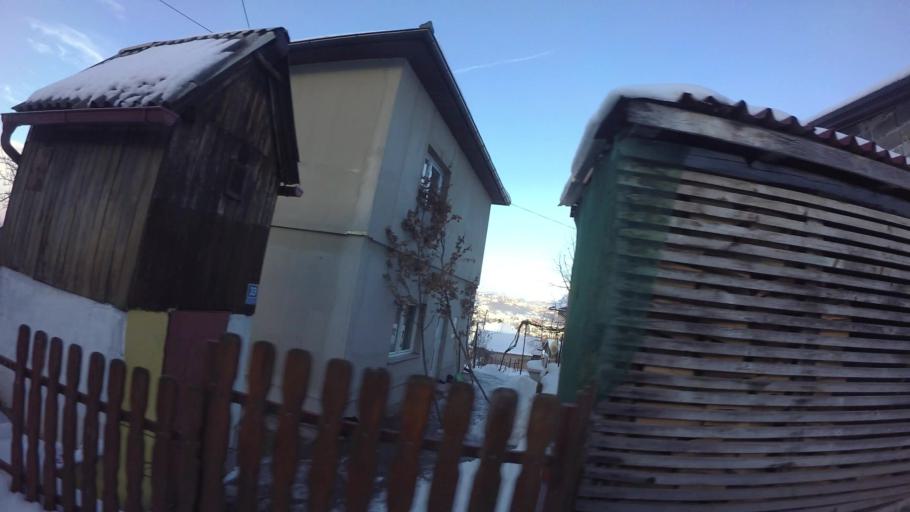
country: BA
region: Federation of Bosnia and Herzegovina
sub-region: Kanton Sarajevo
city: Sarajevo
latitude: 43.8079
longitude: 18.3529
